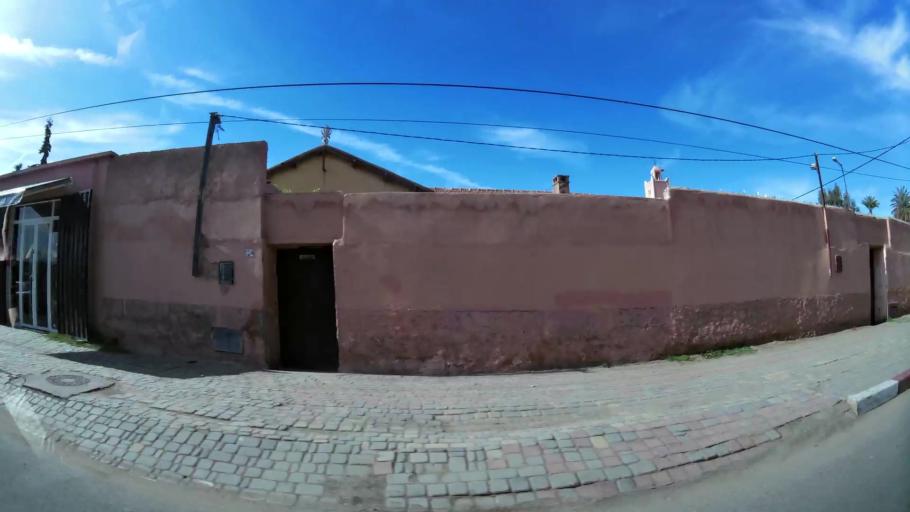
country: MA
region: Marrakech-Tensift-Al Haouz
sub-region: Marrakech
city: Marrakesh
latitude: 31.6433
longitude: -8.0371
